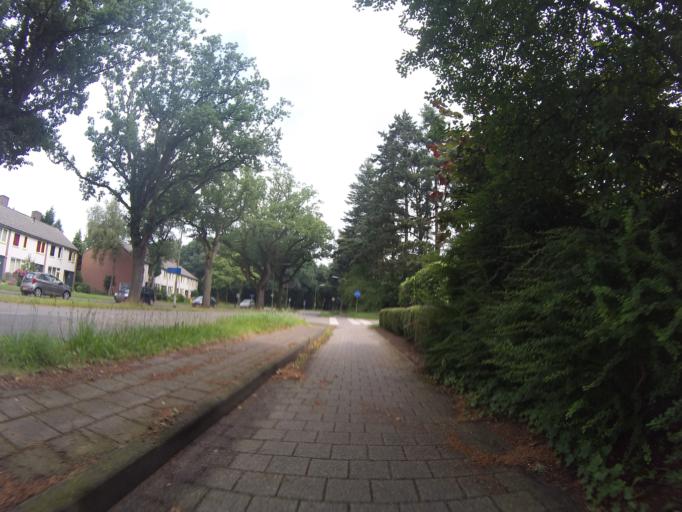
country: NL
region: Drenthe
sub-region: Gemeente Emmen
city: Emmen
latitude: 52.8002
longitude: 6.9021
